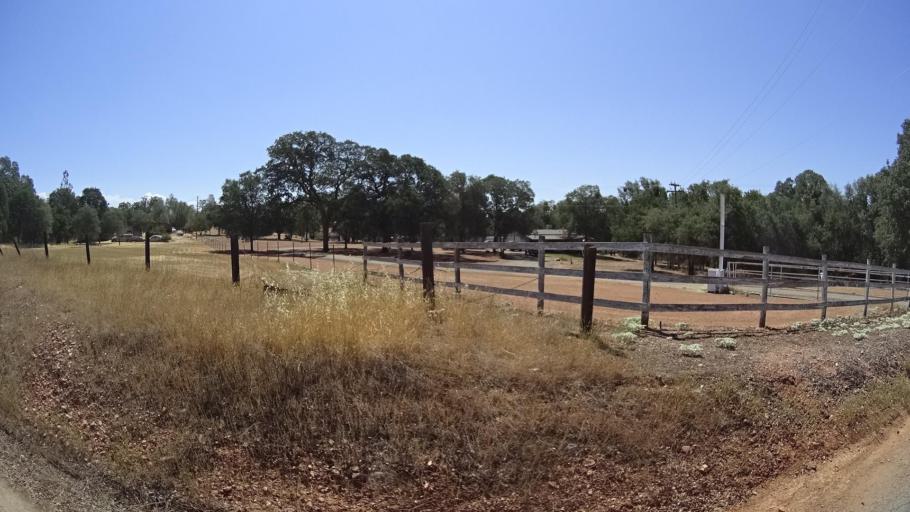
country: US
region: California
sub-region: Mariposa County
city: Mariposa
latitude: 37.4568
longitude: -119.9138
